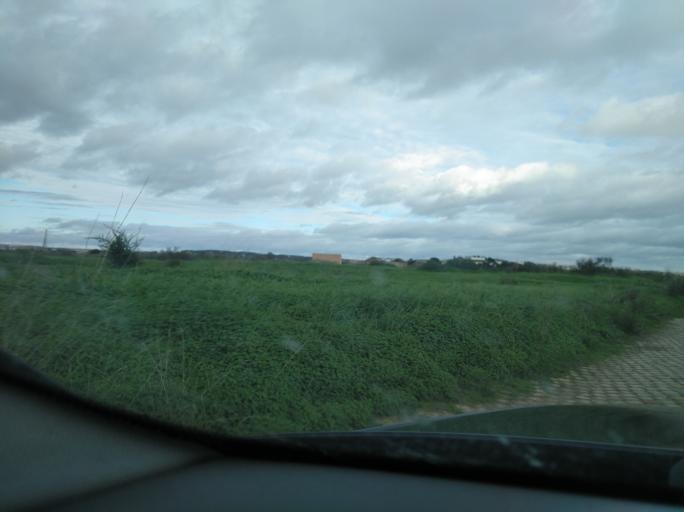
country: PT
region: Faro
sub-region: Castro Marim
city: Castro Marim
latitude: 37.2185
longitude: -7.4348
